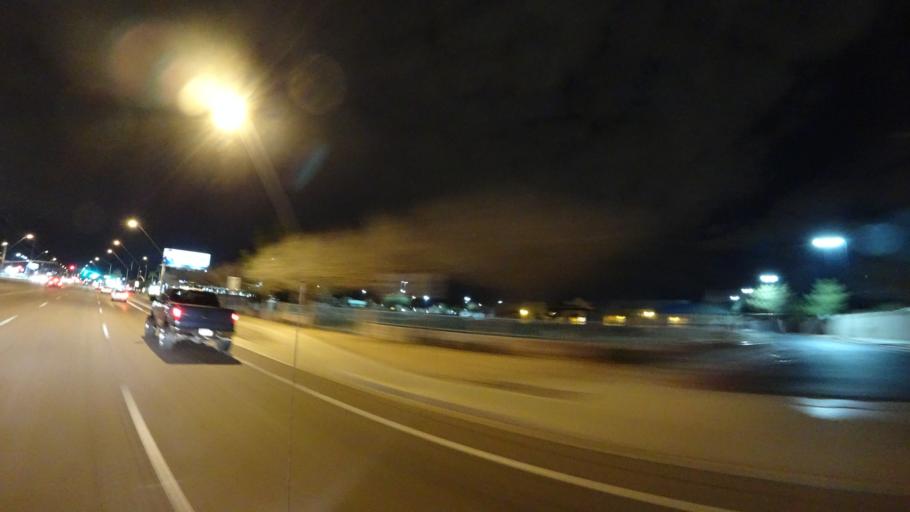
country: US
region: Arizona
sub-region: Maricopa County
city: Mesa
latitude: 33.4060
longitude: -111.8567
